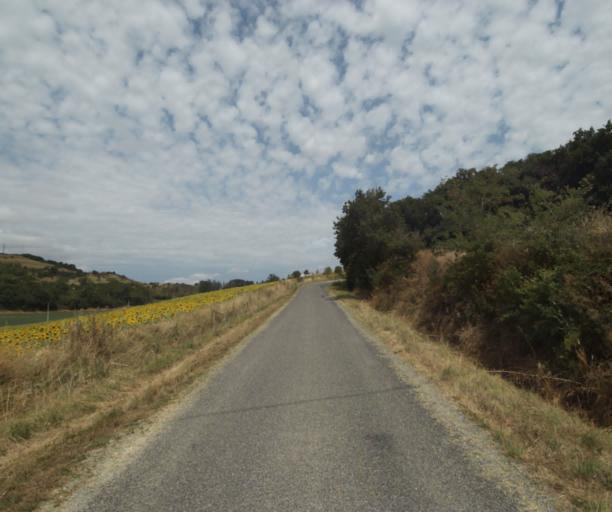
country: FR
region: Midi-Pyrenees
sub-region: Departement de la Haute-Garonne
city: Saint-Felix-Lauragais
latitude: 43.4372
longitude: 1.8932
